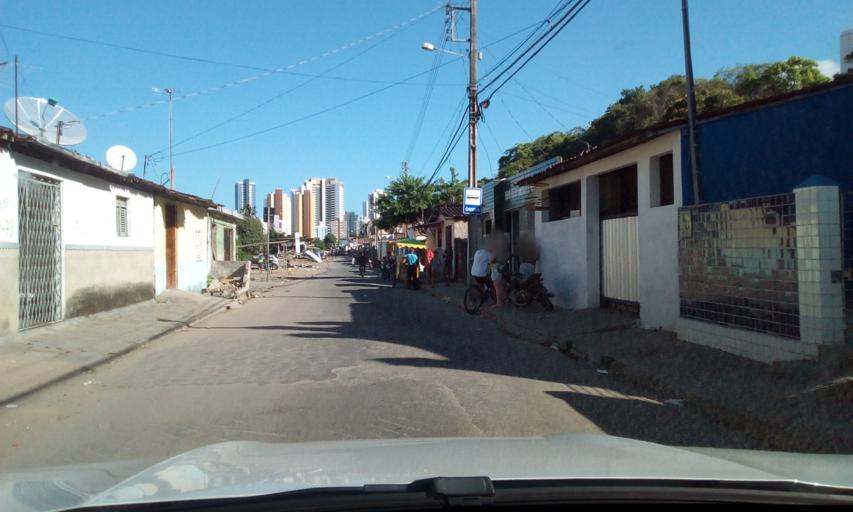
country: BR
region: Paraiba
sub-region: Joao Pessoa
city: Joao Pessoa
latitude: -7.1110
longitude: -34.8370
